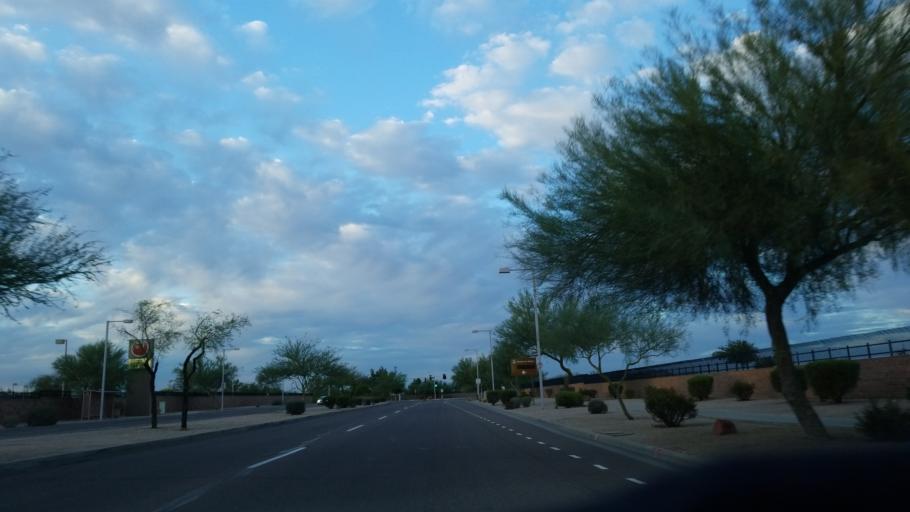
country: US
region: Arizona
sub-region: Maricopa County
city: Phoenix
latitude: 33.4388
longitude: -112.0345
